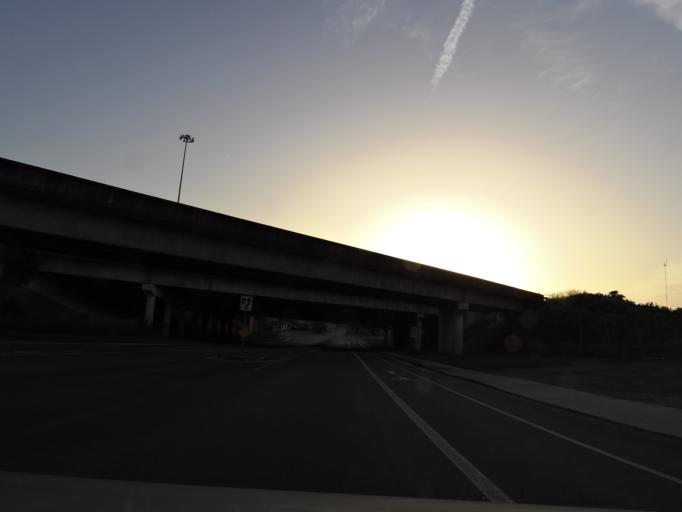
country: US
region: Tennessee
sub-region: Knox County
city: Knoxville
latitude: 35.9711
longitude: -83.9294
